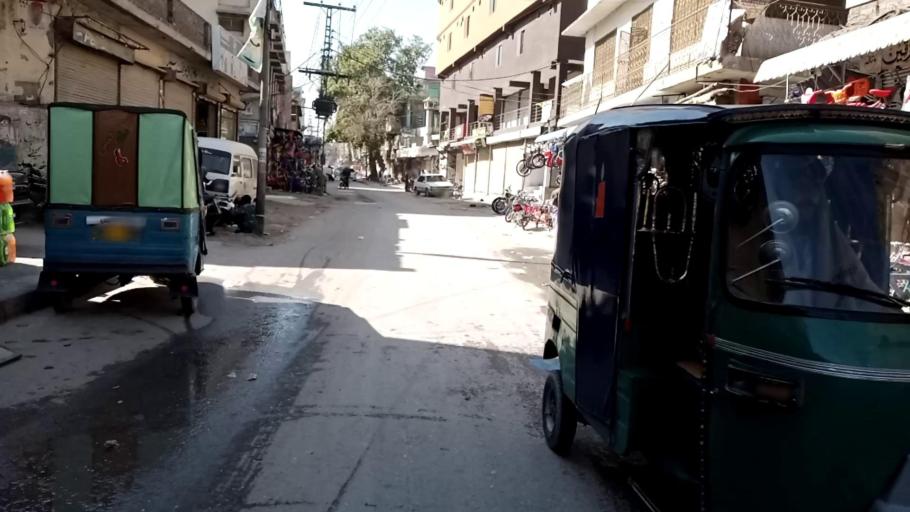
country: PK
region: Khyber Pakhtunkhwa
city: Peshawar
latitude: 34.0146
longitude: 71.5837
